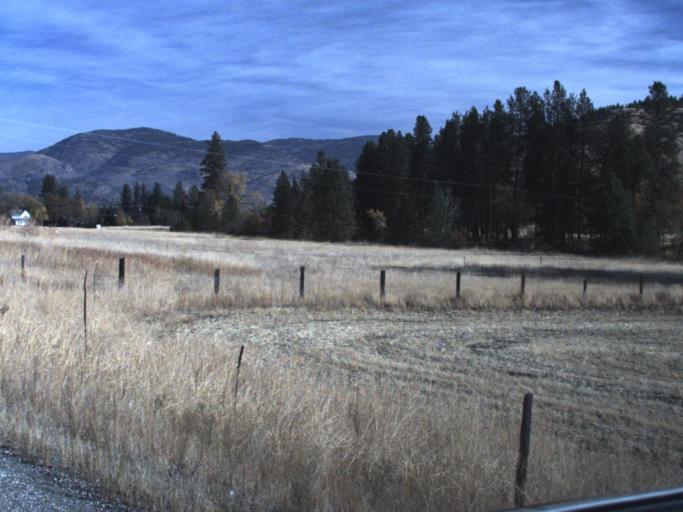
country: CA
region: British Columbia
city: Grand Forks
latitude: 48.9968
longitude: -118.5050
